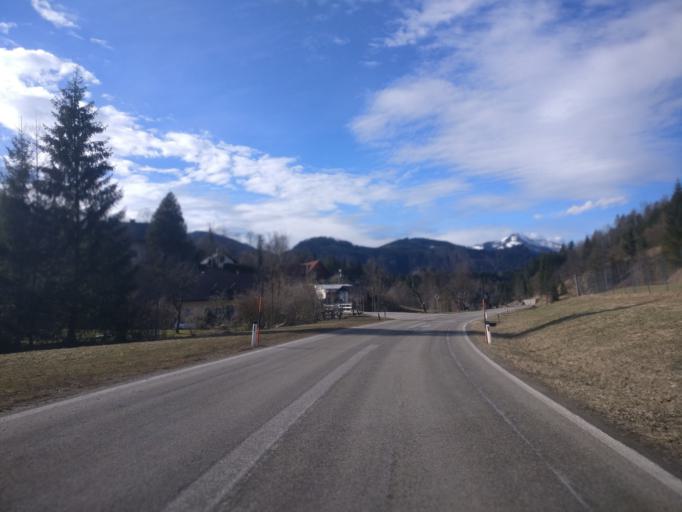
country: AT
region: Styria
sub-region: Politischer Bezirk Liezen
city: Sankt Gallen
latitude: 47.6790
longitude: 14.6337
